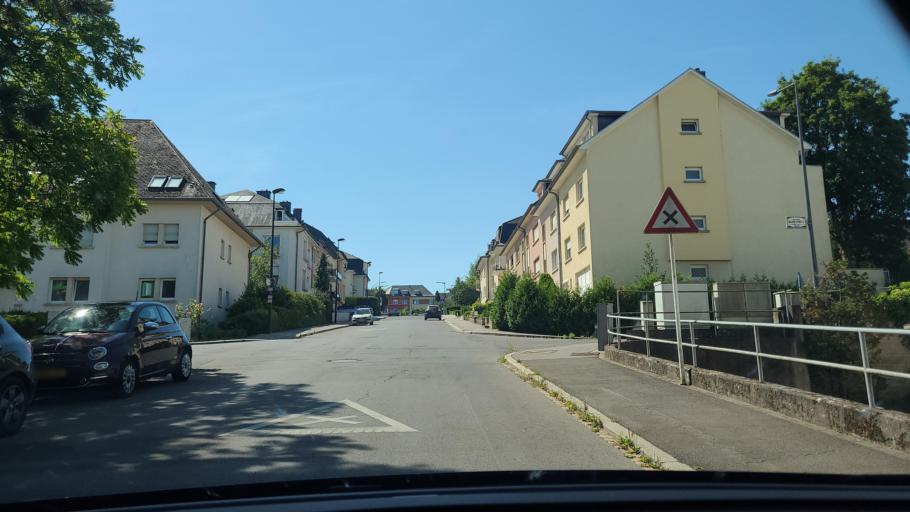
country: LU
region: Luxembourg
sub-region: Canton de Luxembourg
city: Luxembourg
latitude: 49.6000
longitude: 6.1491
